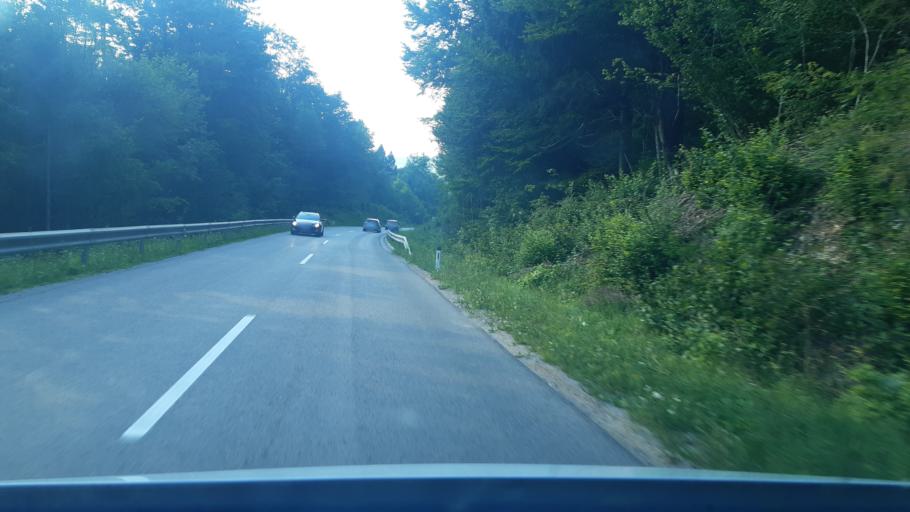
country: SI
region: Semic
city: Semic
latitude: 45.6577
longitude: 15.1172
